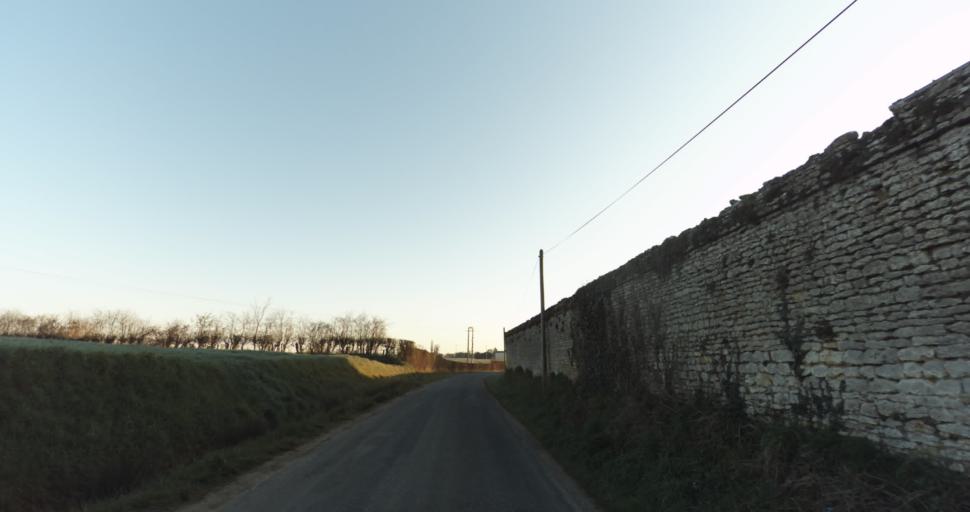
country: FR
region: Lower Normandy
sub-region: Departement du Calvados
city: Saint-Pierre-sur-Dives
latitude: 49.0270
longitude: -0.0348
